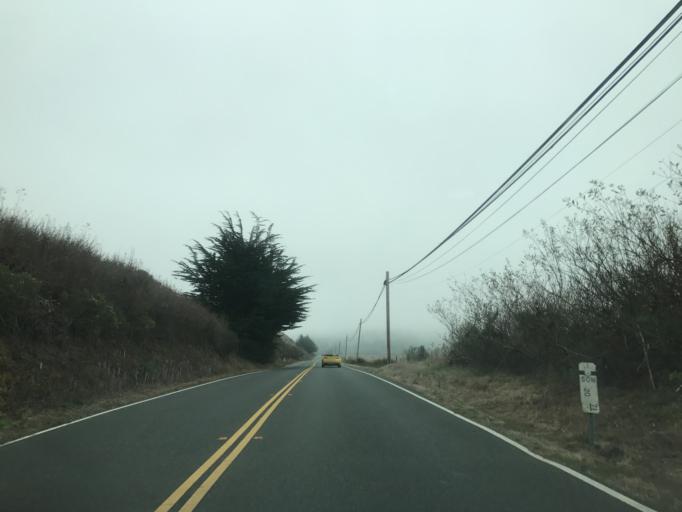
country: US
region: California
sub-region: Sonoma County
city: Monte Rio
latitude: 38.4440
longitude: -123.1106
